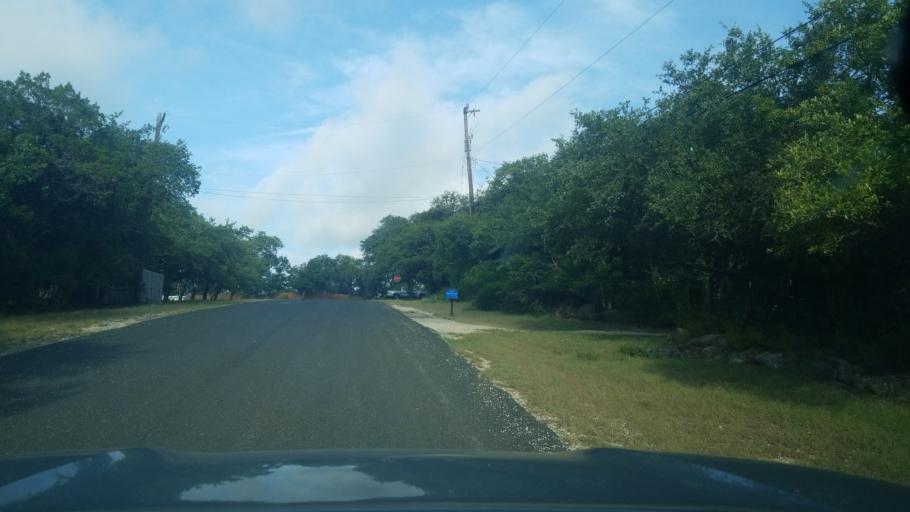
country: US
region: Texas
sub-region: Bexar County
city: Timberwood Park
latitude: 29.6999
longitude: -98.5135
